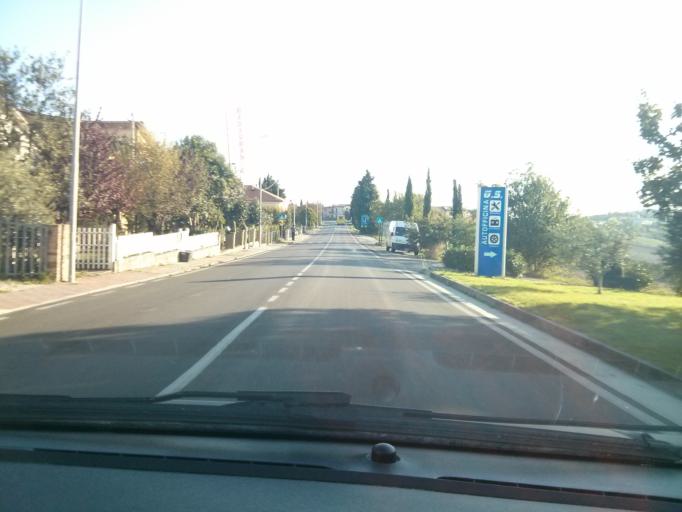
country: IT
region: The Marches
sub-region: Provincia di Pesaro e Urbino
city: San Giorgio di Pesaro
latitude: 43.7070
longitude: 12.9842
